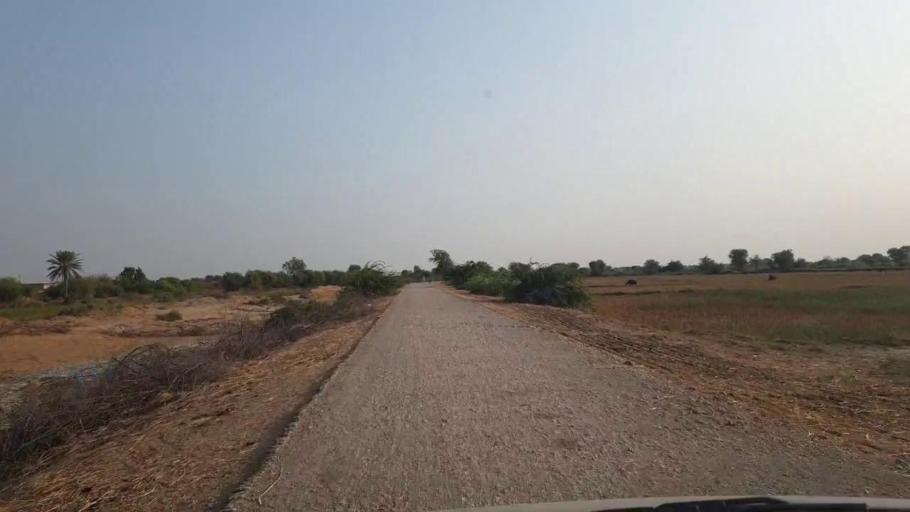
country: PK
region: Sindh
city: Rajo Khanani
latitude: 25.0153
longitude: 68.7864
